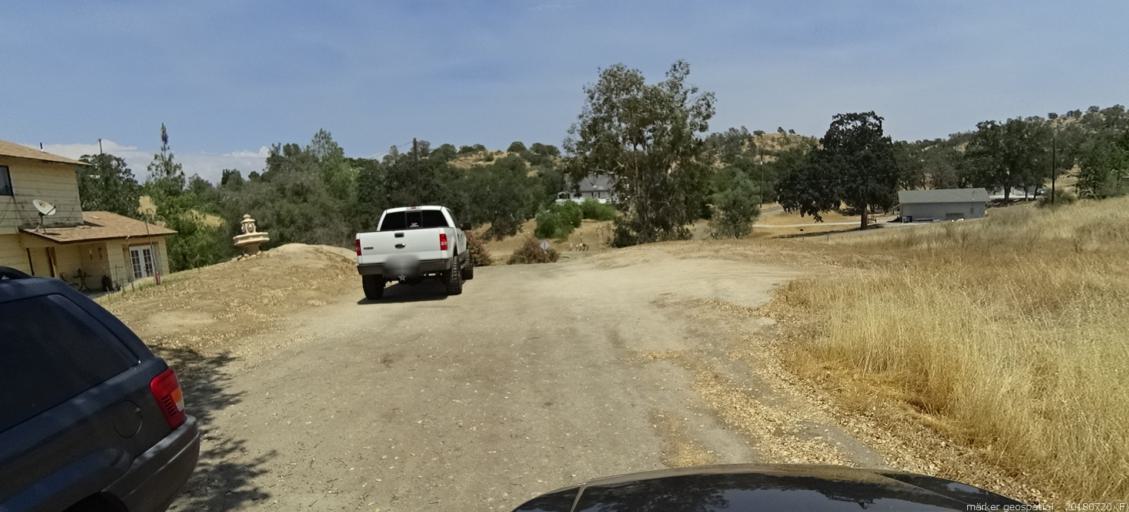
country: US
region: California
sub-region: Madera County
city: Yosemite Lakes
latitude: 37.1600
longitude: -119.8482
